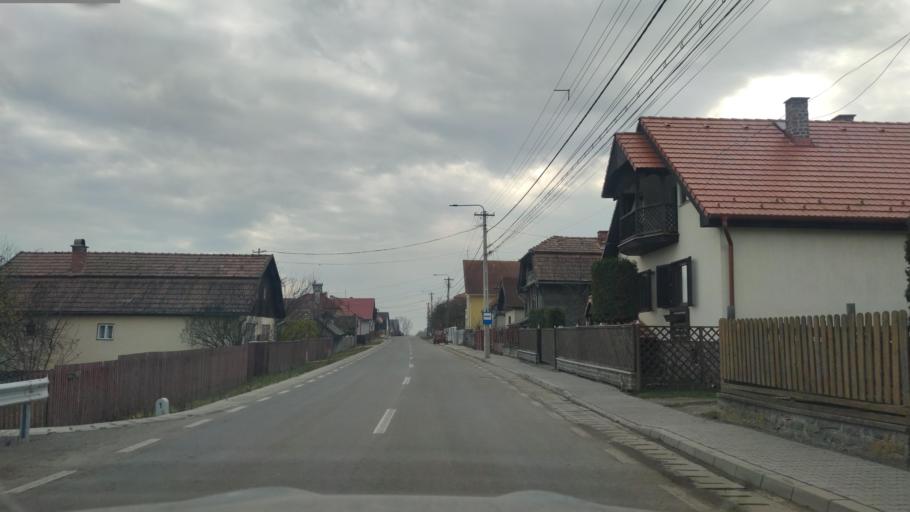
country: RO
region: Harghita
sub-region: Comuna Remetea
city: Remetea
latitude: 46.8084
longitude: 25.4597
